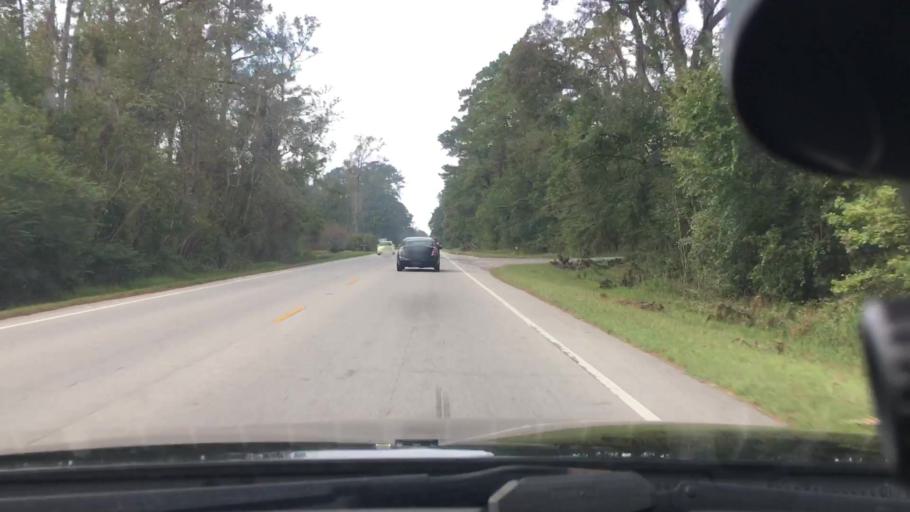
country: US
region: North Carolina
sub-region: Craven County
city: New Bern
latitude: 35.1658
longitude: -77.0408
